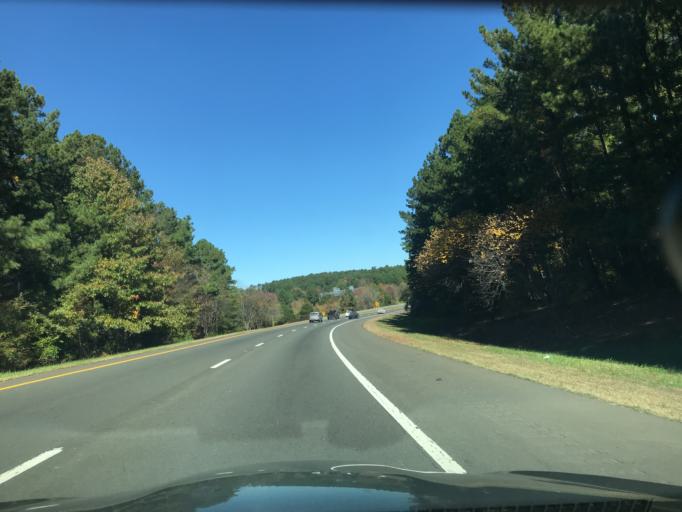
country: US
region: North Carolina
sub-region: Wake County
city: Morrisville
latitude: 35.9023
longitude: -78.8708
